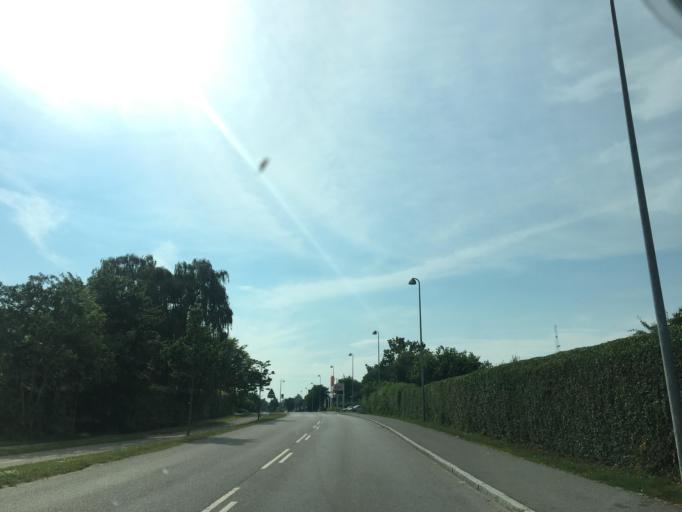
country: DK
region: Zealand
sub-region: Greve Kommune
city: Tune
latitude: 55.5962
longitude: 12.1912
